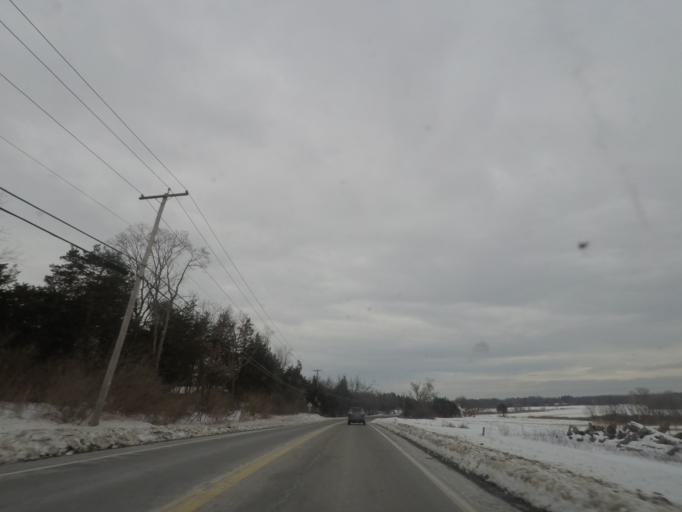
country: US
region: New York
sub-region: Columbia County
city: Kinderhook
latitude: 42.3723
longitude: -73.7327
